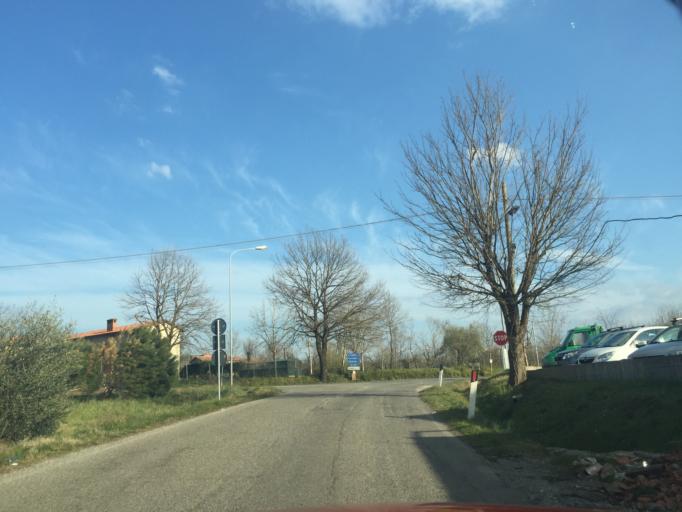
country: IT
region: Tuscany
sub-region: Province of Florence
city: Stabbia
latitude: 43.7736
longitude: 10.8300
